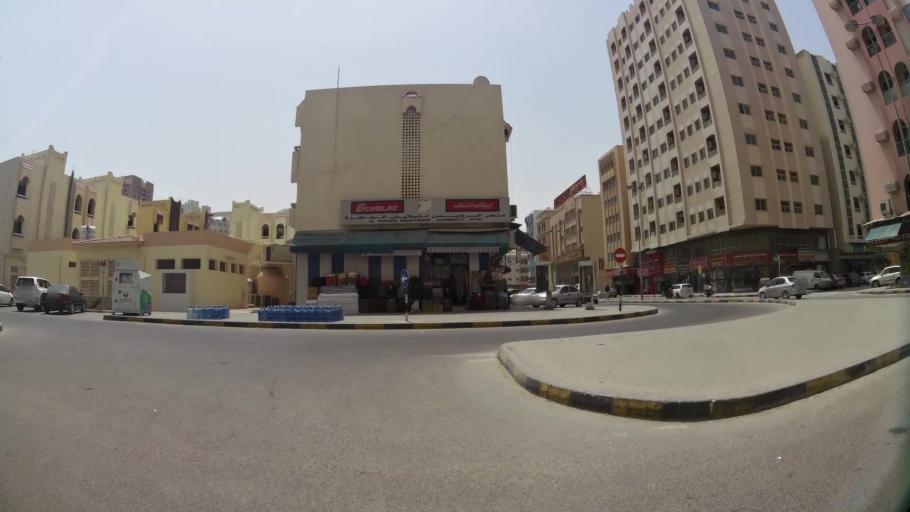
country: AE
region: Ash Shariqah
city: Sharjah
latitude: 25.3582
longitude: 55.3913
